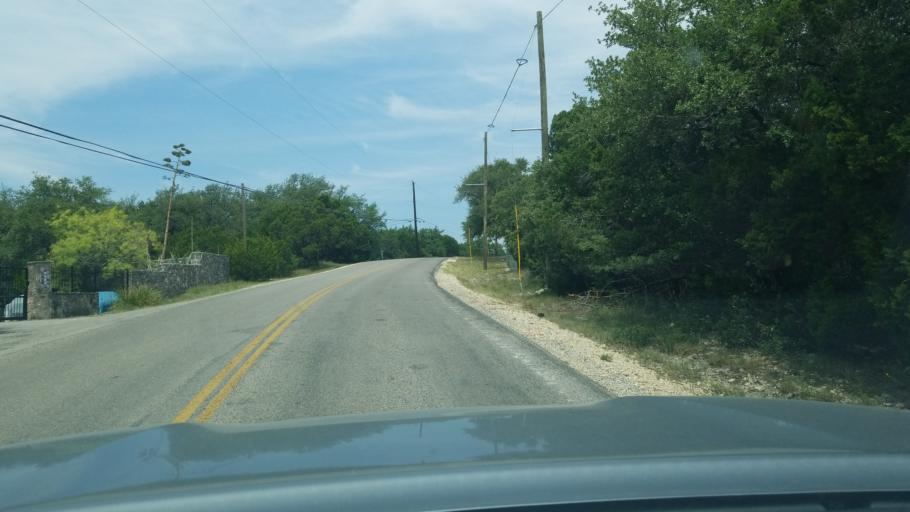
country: US
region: Texas
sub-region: Comal County
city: Bulverde
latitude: 29.7744
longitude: -98.4289
